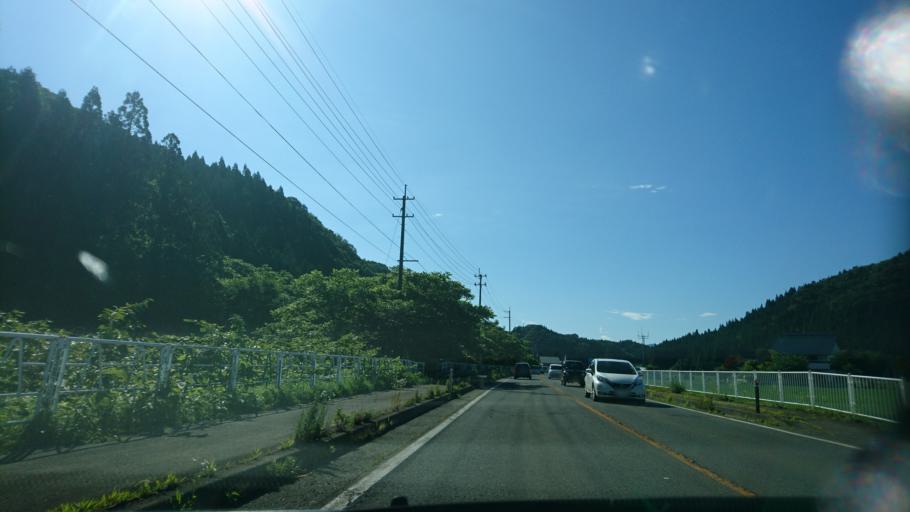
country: JP
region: Akita
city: Kakunodatemachi
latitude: 39.6000
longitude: 140.5240
